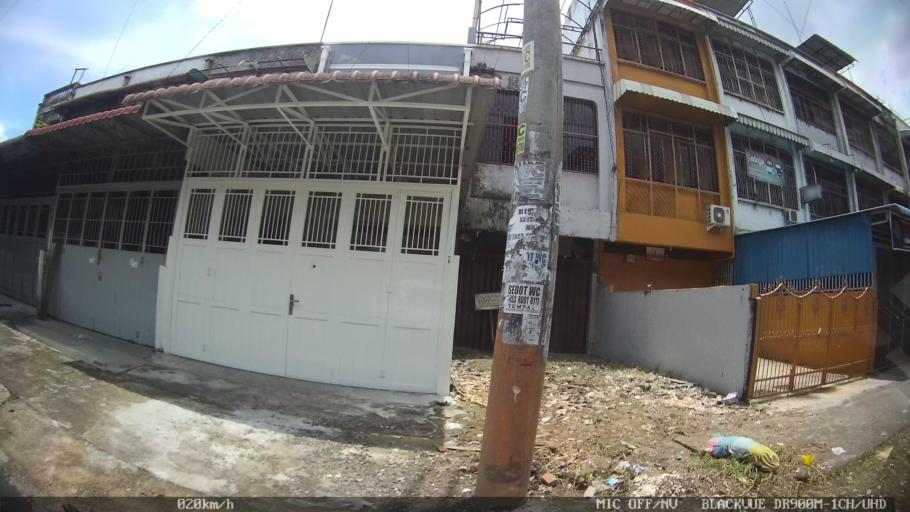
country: ID
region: North Sumatra
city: Medan
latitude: 3.6259
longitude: 98.6704
